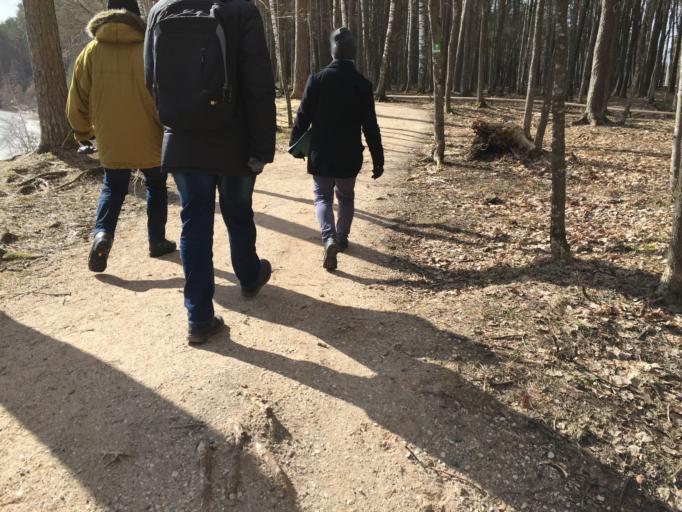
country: LV
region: Valmieras Rajons
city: Valmiera
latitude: 57.5414
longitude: 25.4448
